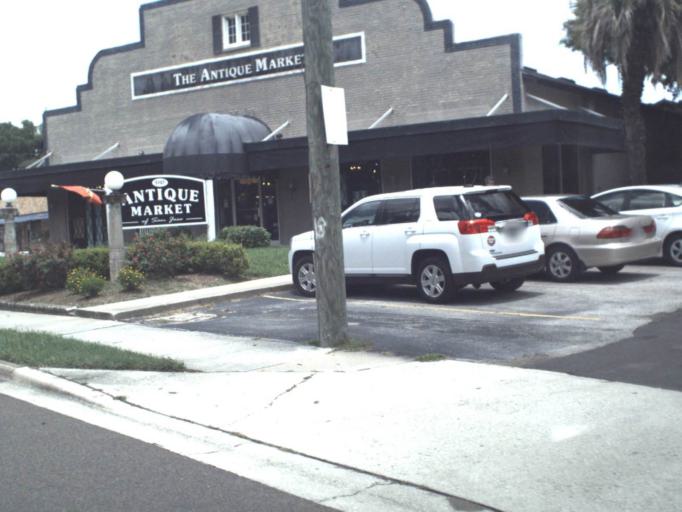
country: US
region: Florida
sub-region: Duval County
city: Jacksonville
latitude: 30.2652
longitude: -81.6472
